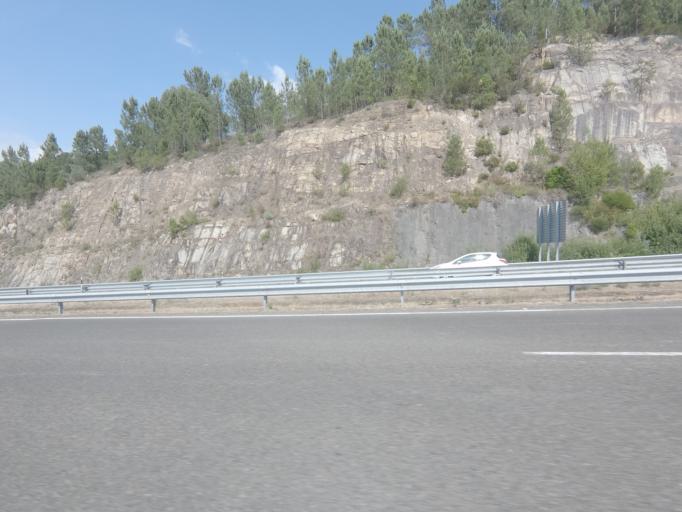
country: ES
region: Galicia
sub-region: Provincia de Ourense
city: Ourense
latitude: 42.2947
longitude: -7.8777
